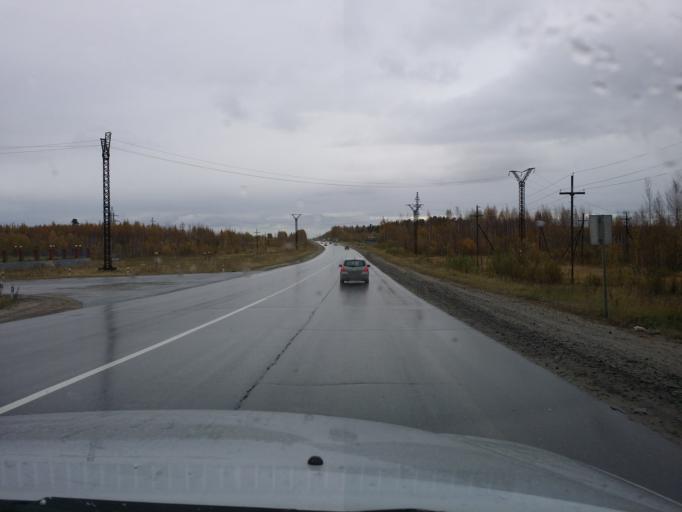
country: RU
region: Khanty-Mansiyskiy Avtonomnyy Okrug
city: Megion
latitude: 61.0572
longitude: 76.1143
